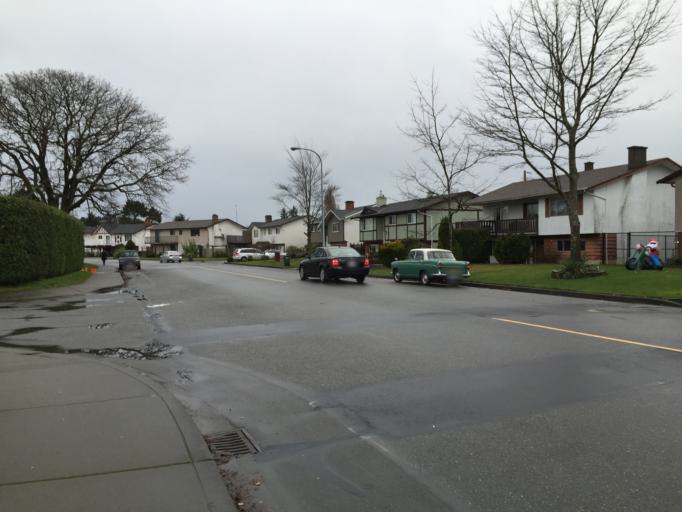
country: CA
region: British Columbia
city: Oak Bay
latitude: 48.4711
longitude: -123.3251
